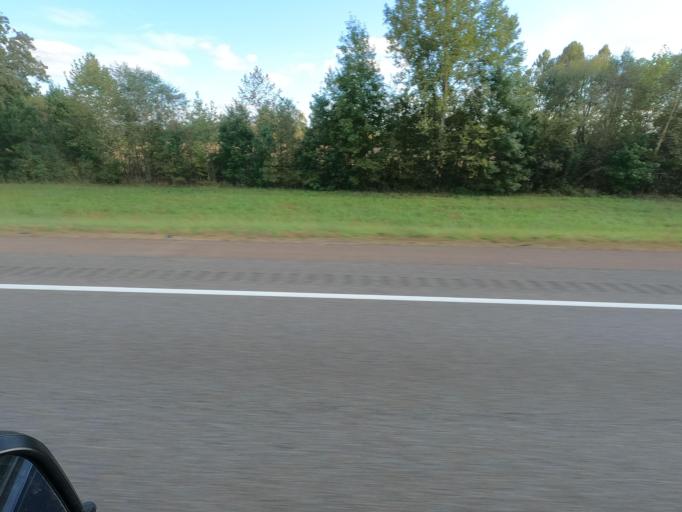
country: US
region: Tennessee
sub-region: Henderson County
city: Lexington
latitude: 35.7757
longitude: -88.4304
